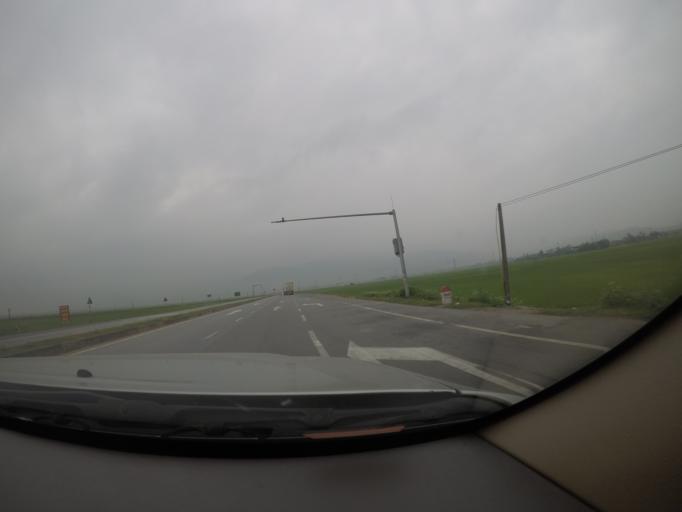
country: VN
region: Ha Tinh
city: Ky Anh
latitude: 18.1067
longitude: 106.2669
